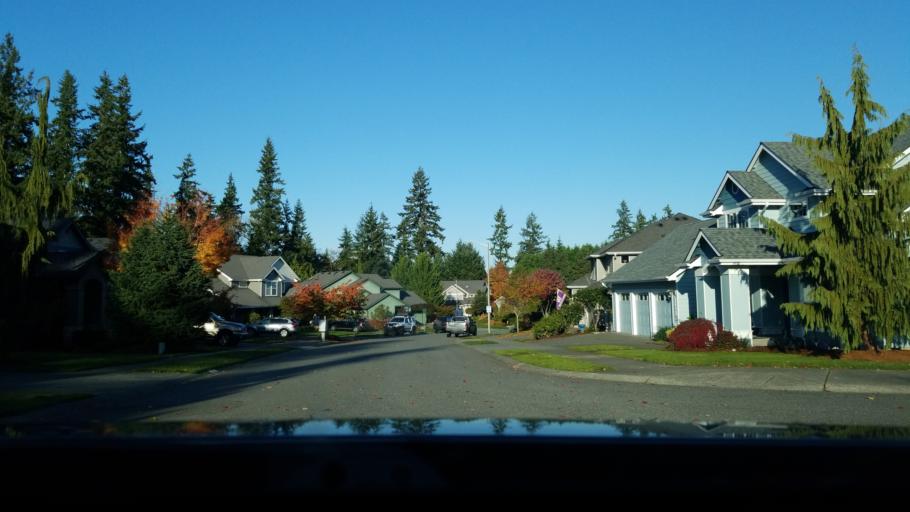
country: US
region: Washington
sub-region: Snohomish County
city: Silver Firs
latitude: 47.8930
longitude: -122.1778
